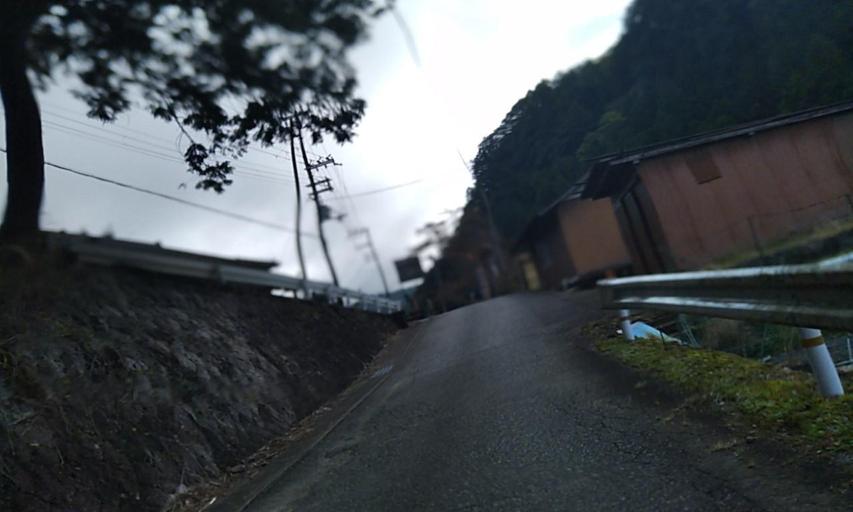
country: JP
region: Wakayama
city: Shingu
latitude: 33.9330
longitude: 135.9743
